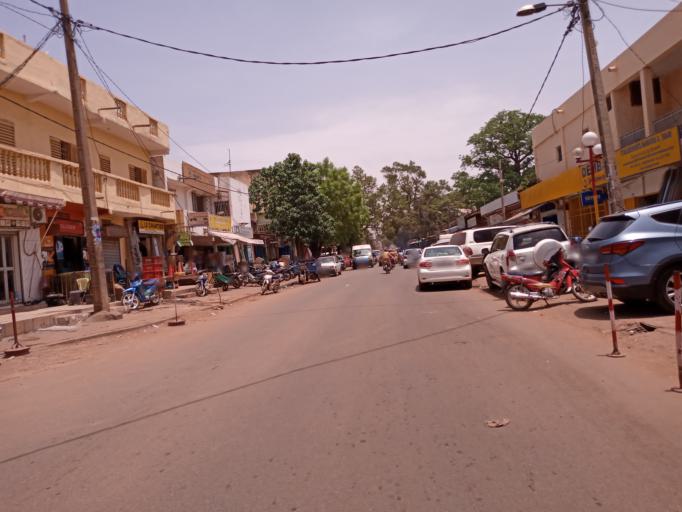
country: ML
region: Bamako
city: Bamako
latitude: 12.6404
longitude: -8.0013
